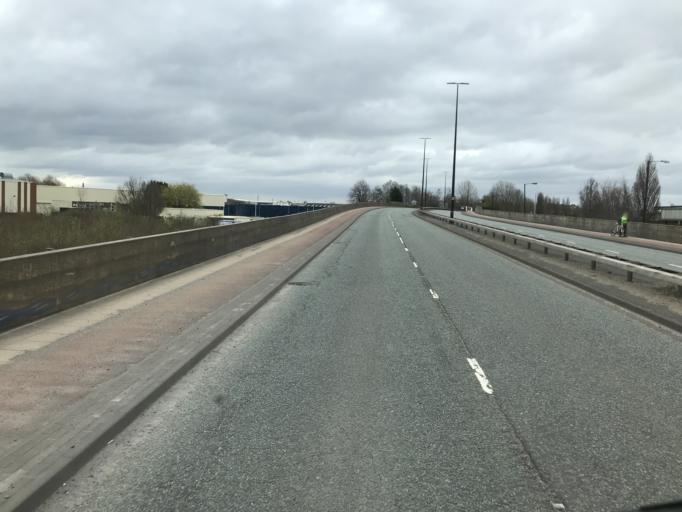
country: GB
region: England
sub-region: City and Borough of Salford
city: Eccles
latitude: 53.4791
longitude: -2.3249
